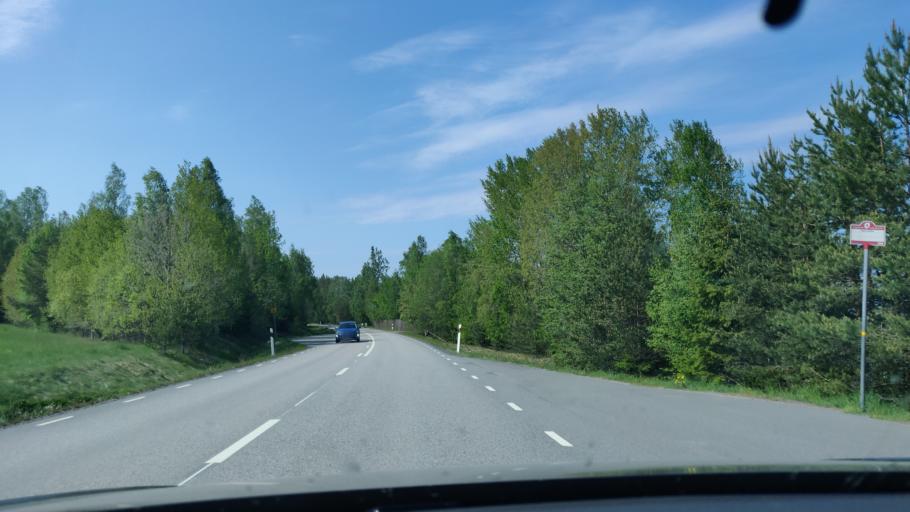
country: SE
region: Uppsala
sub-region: Heby Kommun
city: OEstervala
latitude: 60.1401
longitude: 17.2152
